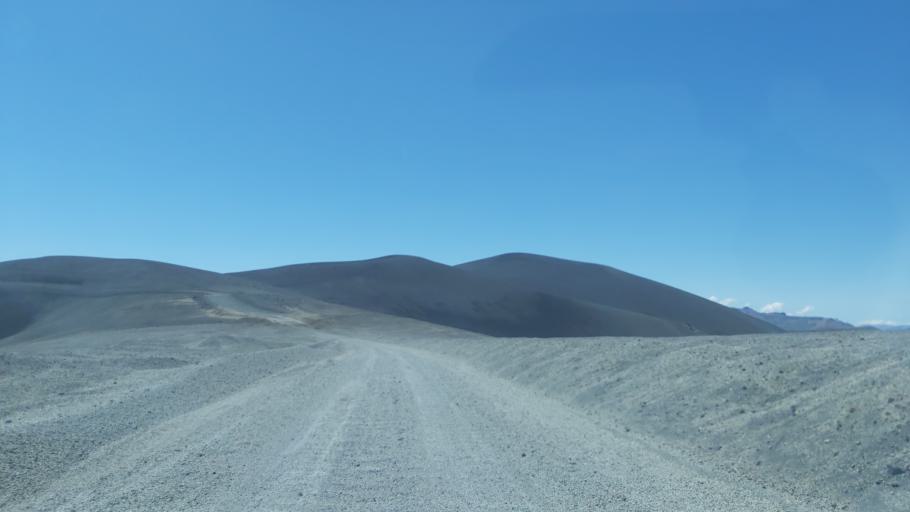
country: CL
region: Araucania
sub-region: Provincia de Cautin
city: Vilcun
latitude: -38.3768
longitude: -71.5412
